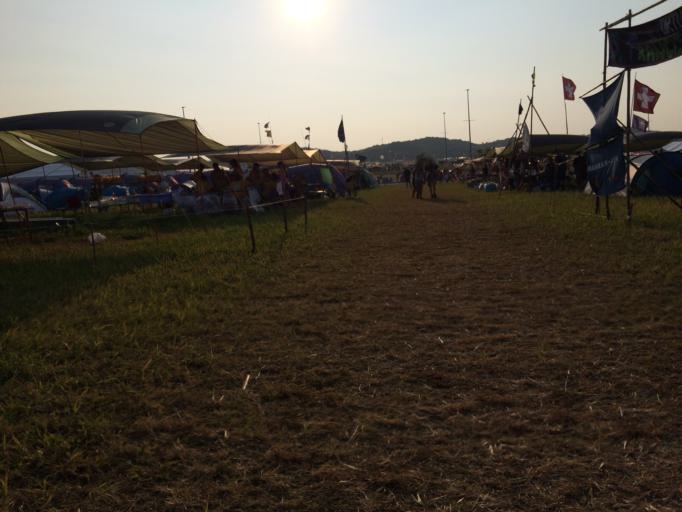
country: JP
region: Yamaguchi
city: Ogori-shimogo
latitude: 34.0147
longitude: 131.3770
